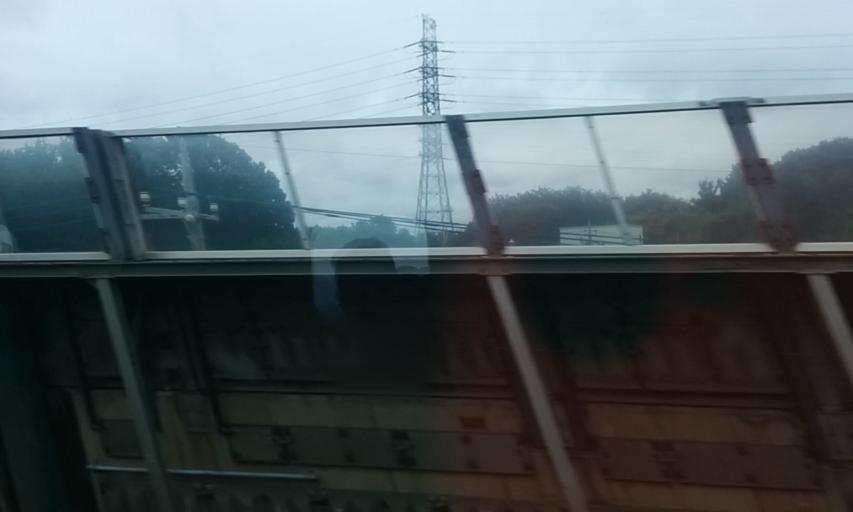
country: JP
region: Tochigi
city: Oyama
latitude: 36.2770
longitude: 139.7779
